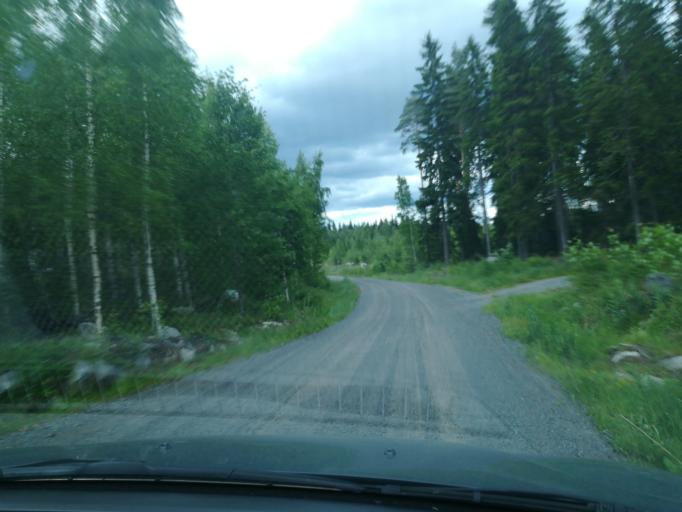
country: FI
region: Southern Savonia
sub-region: Mikkeli
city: Mikkeli
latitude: 61.6669
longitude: 27.1198
